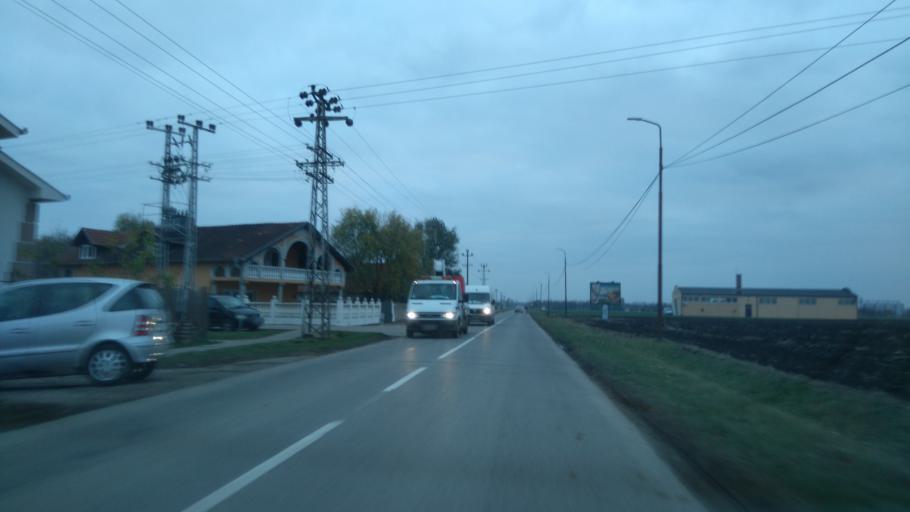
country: RS
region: Autonomna Pokrajina Vojvodina
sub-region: Severnobanatski Okrug
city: Ada
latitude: 45.7859
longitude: 20.1275
